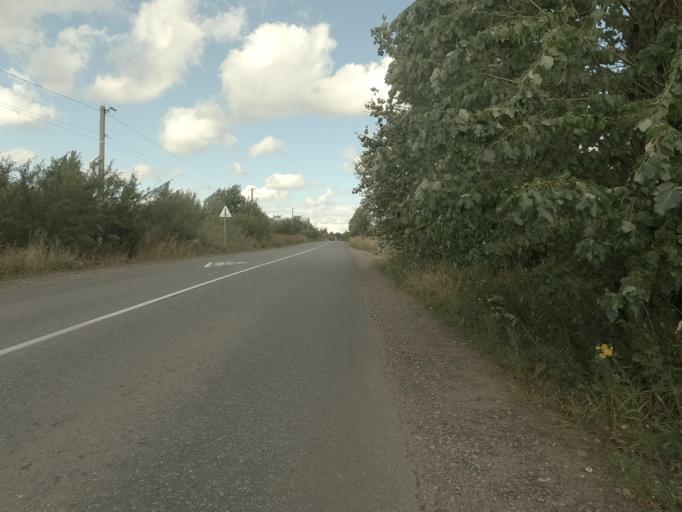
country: RU
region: Leningrad
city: Shcheglovo
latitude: 60.0206
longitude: 30.7460
